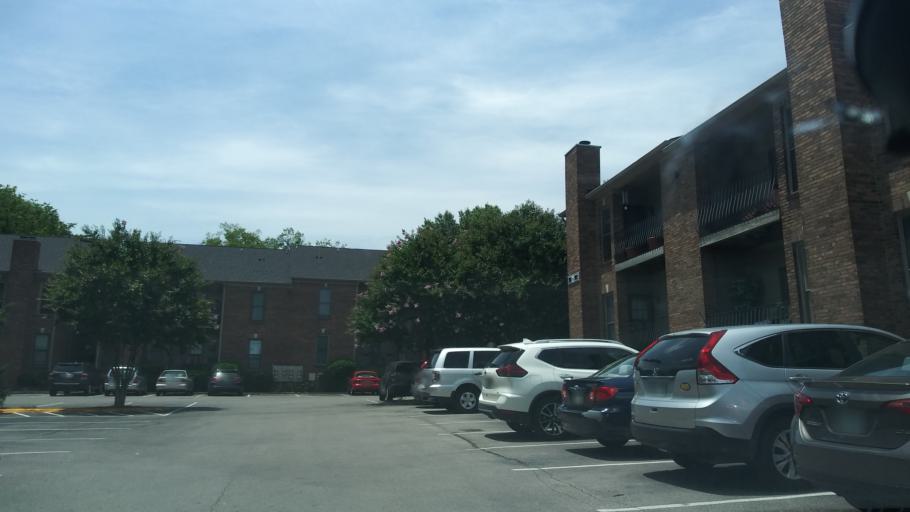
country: US
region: Tennessee
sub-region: Davidson County
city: Belle Meade
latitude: 36.1395
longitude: -86.8413
